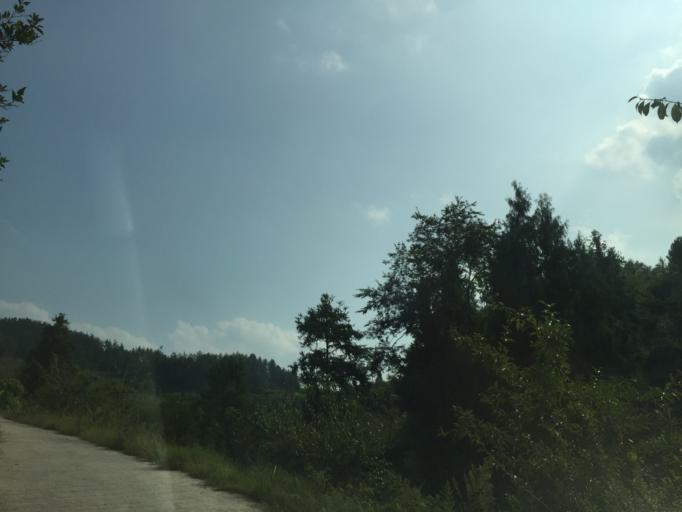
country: CN
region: Guizhou Sheng
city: Jingjiao
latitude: 28.3617
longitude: 108.1181
